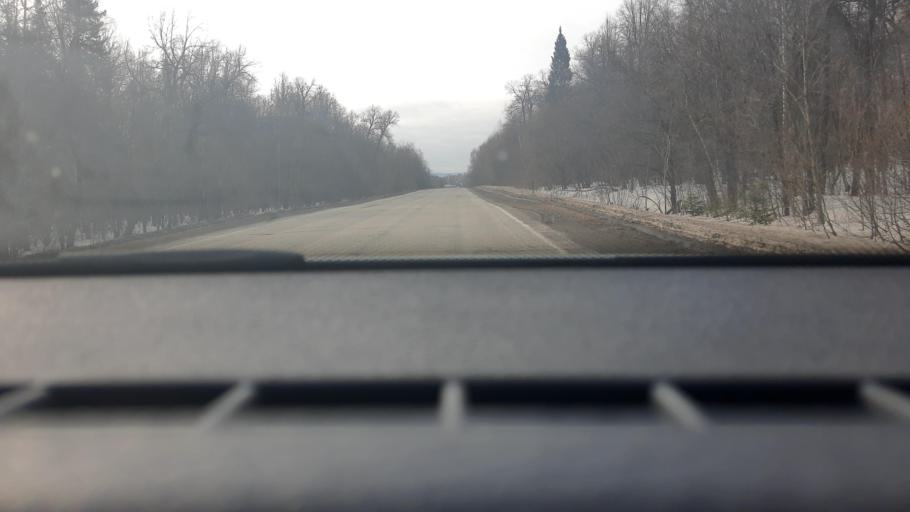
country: RU
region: Chelyabinsk
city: Asha
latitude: 54.8982
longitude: 57.2976
